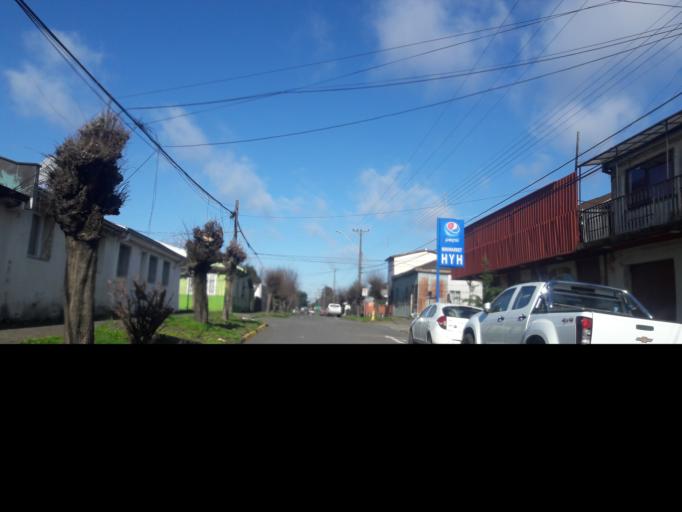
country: CL
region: Araucania
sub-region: Provincia de Malleco
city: Victoria
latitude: -38.2372
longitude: -72.3294
